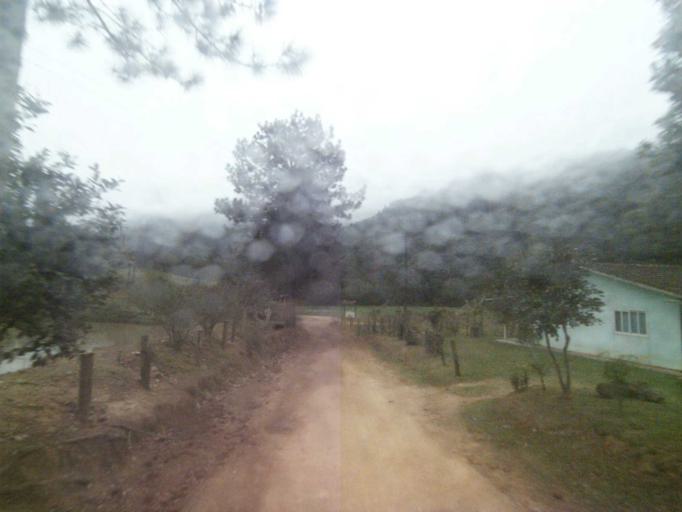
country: BR
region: Santa Catarina
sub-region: Anitapolis
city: Anitapolis
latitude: -27.8820
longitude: -49.1326
